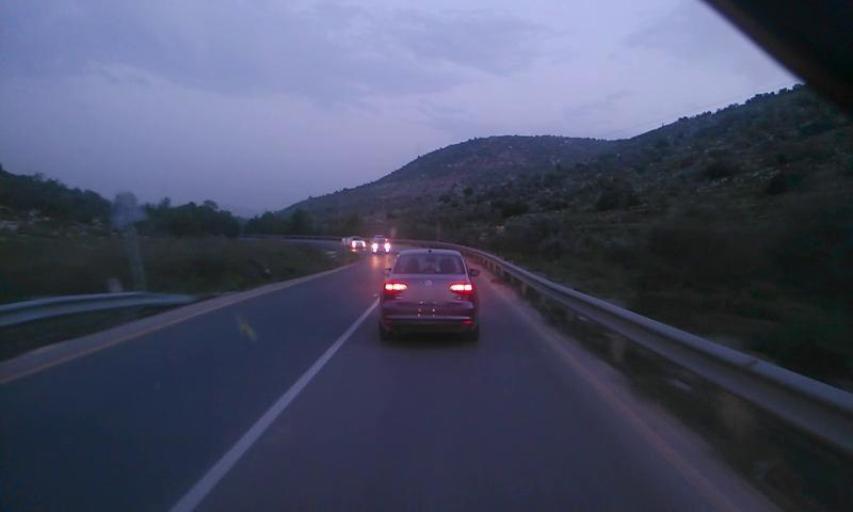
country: PS
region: West Bank
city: Ramin
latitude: 32.2855
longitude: 35.1373
